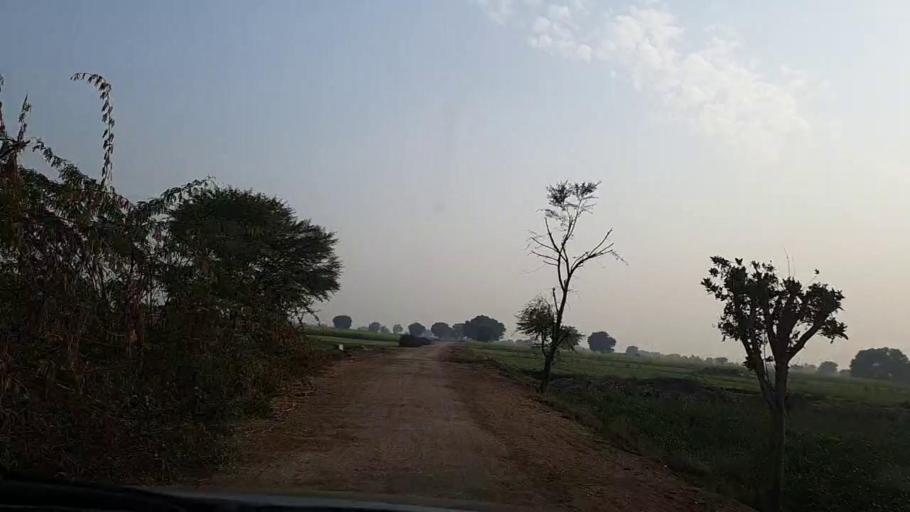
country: PK
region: Sindh
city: Nawabshah
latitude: 26.2721
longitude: 68.3235
